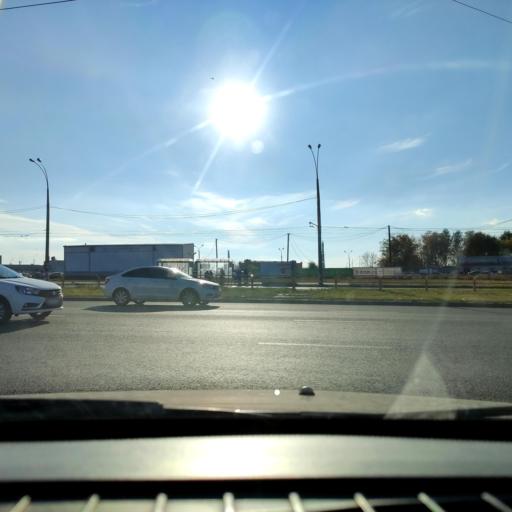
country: RU
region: Samara
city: Tol'yatti
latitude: 53.5538
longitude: 49.2612
